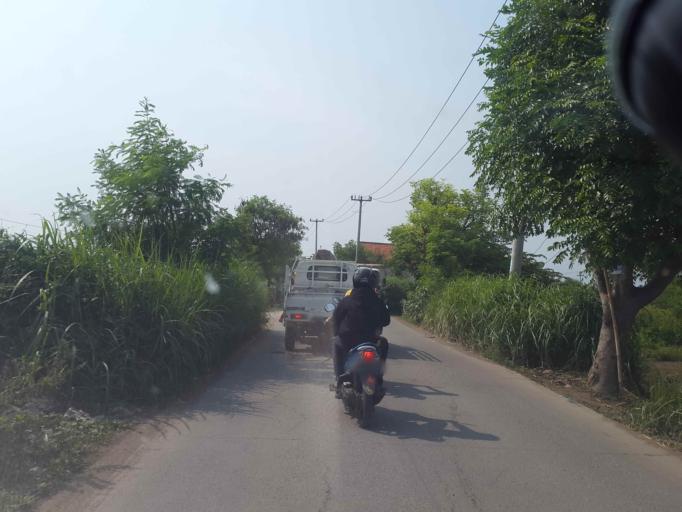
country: ID
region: West Java
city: Cikarang
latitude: -6.2169
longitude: 107.1566
